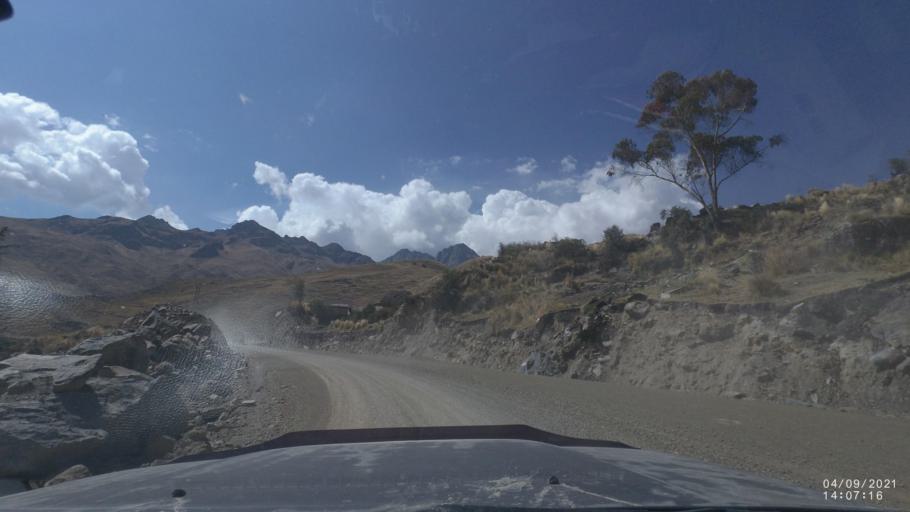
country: BO
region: Cochabamba
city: Sipe Sipe
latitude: -17.2283
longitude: -66.4673
